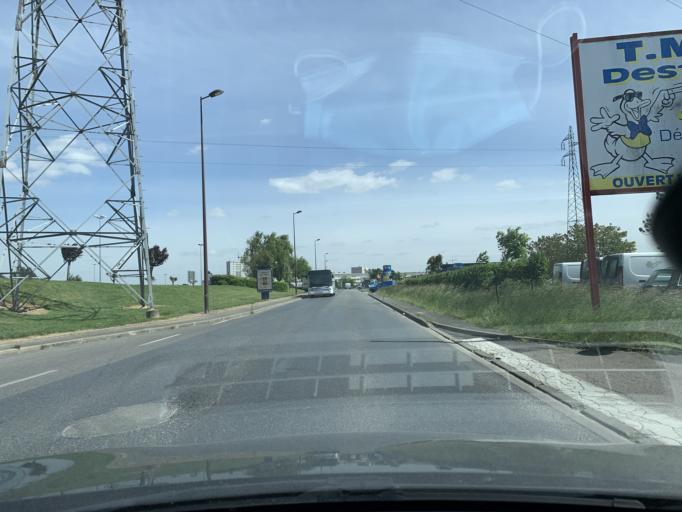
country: FR
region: Picardie
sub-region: Departement de l'Aisne
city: Saint-Quentin
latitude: 49.8657
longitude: 3.2885
